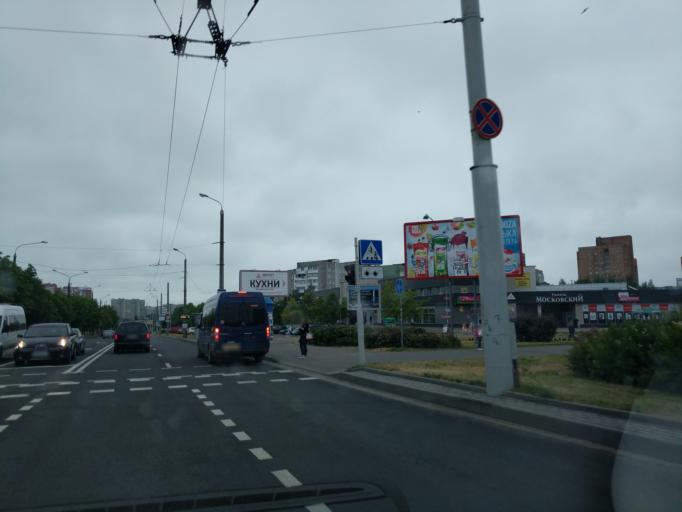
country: BY
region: Minsk
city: Novoye Medvezhino
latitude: 53.8656
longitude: 27.4693
